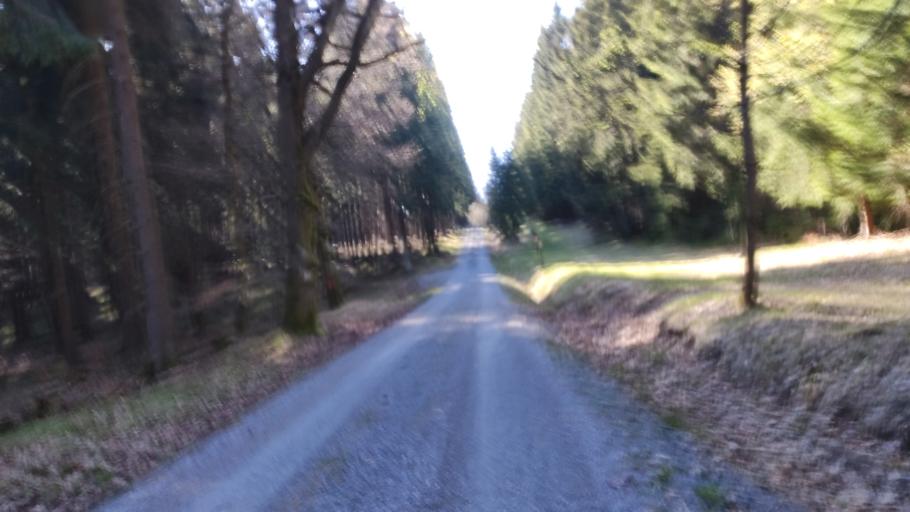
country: DE
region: Bavaria
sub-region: Upper Franconia
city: Reichenbach
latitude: 50.4413
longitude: 11.4450
